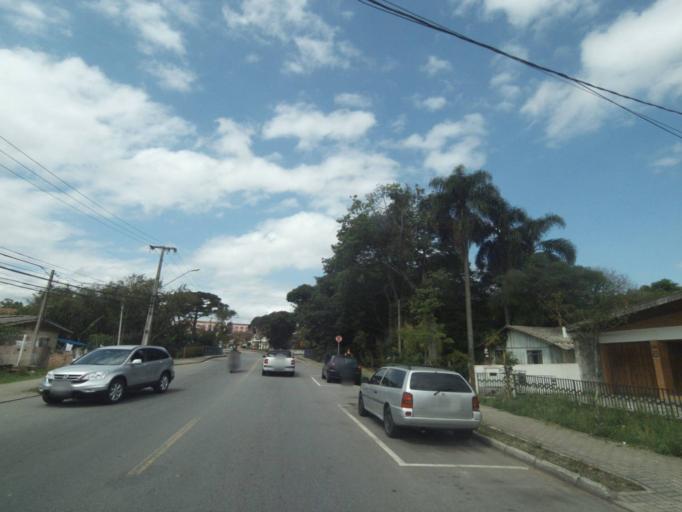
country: BR
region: Parana
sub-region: Pinhais
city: Pinhais
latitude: -25.4140
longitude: -49.2182
